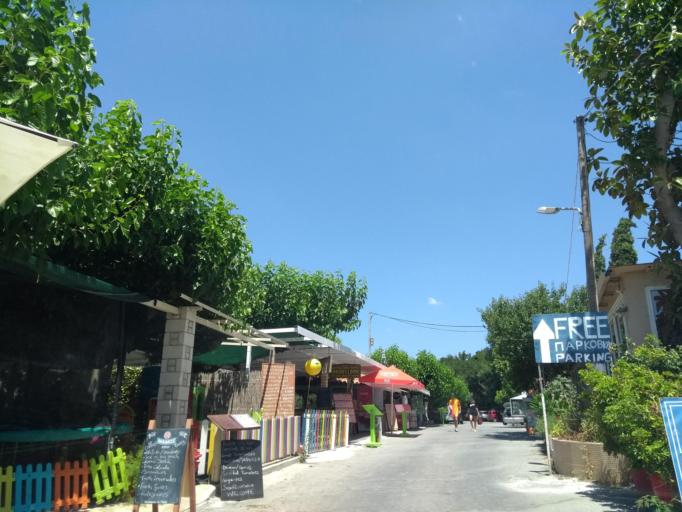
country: GR
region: Crete
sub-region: Nomos Chanias
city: Georgioupolis
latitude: 35.3326
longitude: 24.2796
